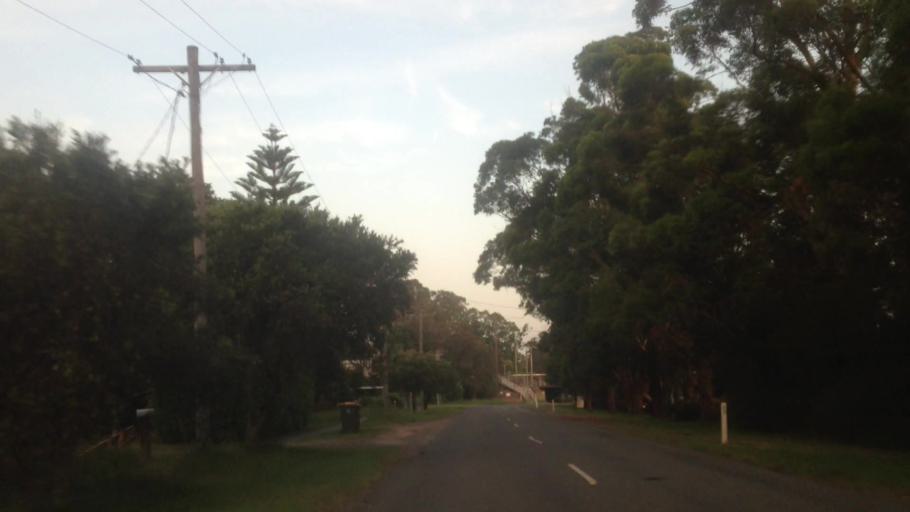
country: AU
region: New South Wales
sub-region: Lake Macquarie Shire
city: Dora Creek
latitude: -33.0828
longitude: 151.4990
